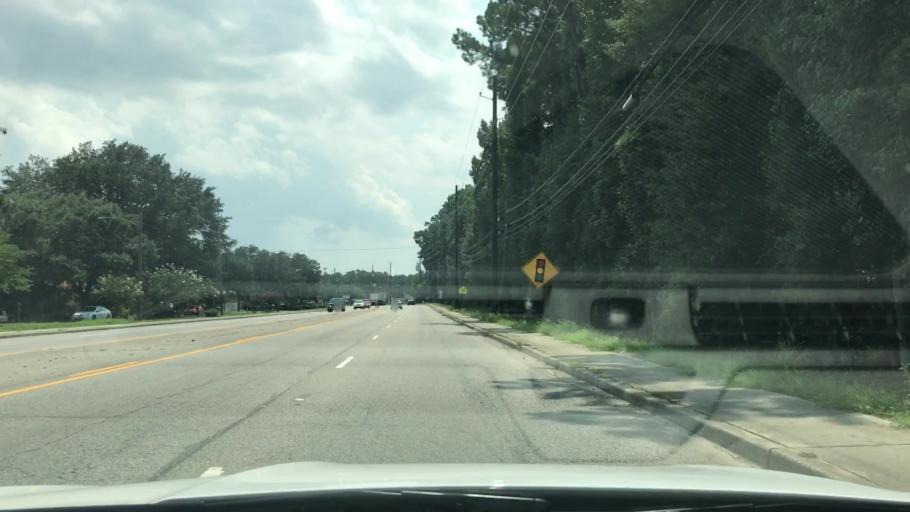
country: US
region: South Carolina
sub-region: Georgetown County
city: Georgetown
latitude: 33.4025
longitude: -79.2888
